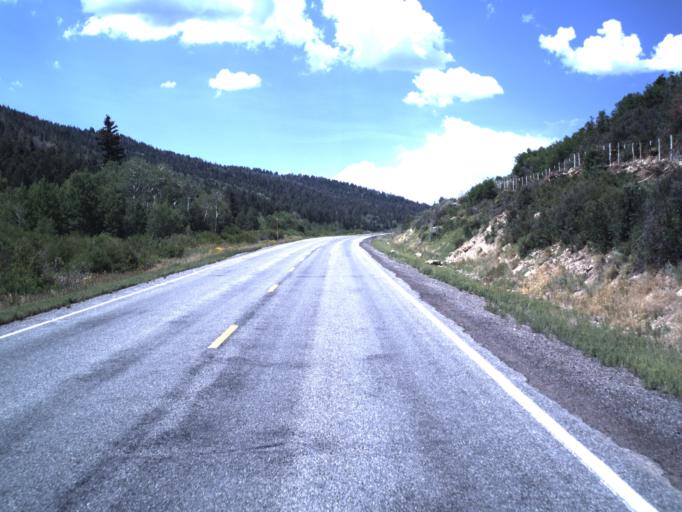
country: US
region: Utah
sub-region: Carbon County
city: Helper
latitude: 39.8569
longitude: -111.0694
